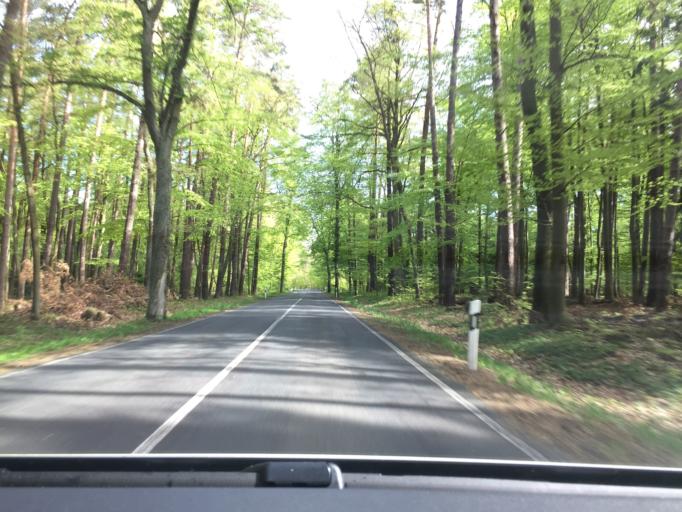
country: DE
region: Mecklenburg-Vorpommern
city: Torgelow
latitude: 53.6593
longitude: 14.0217
